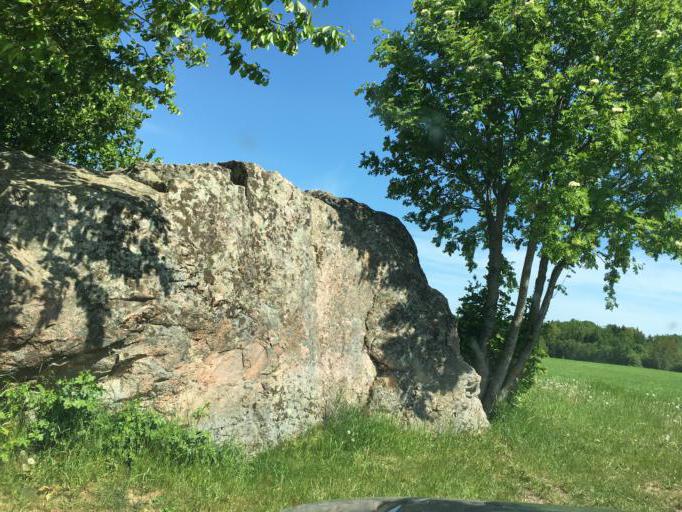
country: LV
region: Talsu Rajons
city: Valdemarpils
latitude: 57.3502
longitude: 22.7227
